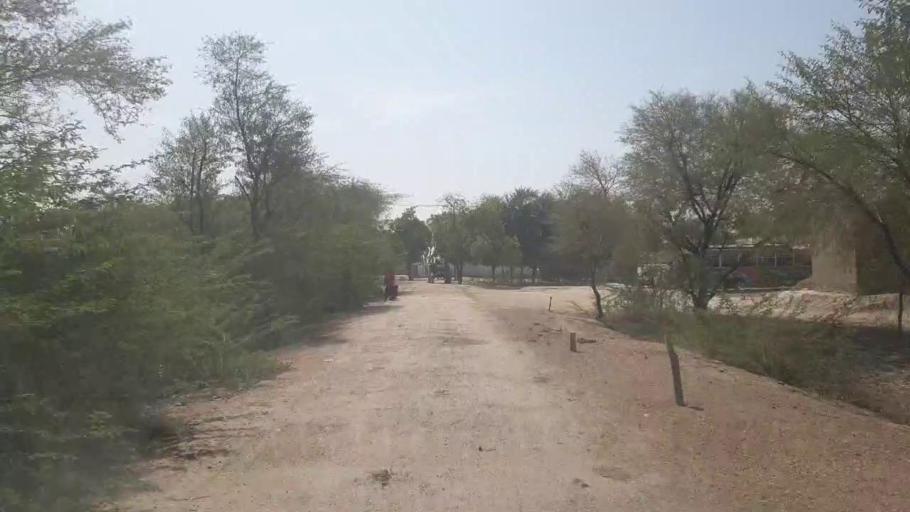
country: PK
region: Sindh
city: Kunri
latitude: 25.2520
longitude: 69.5939
